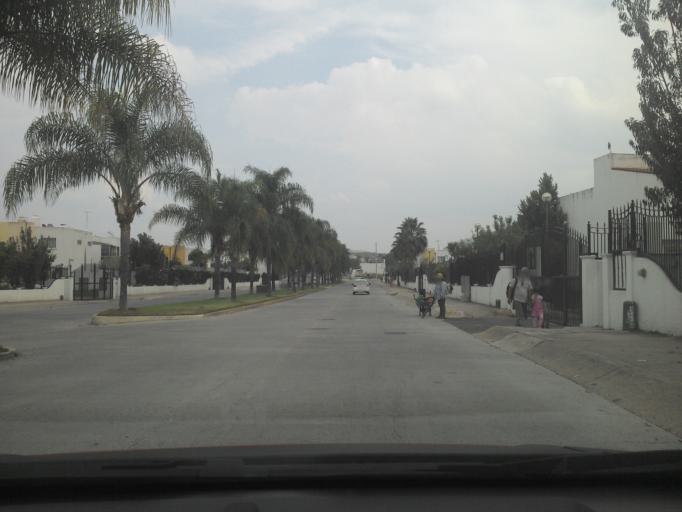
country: MX
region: Jalisco
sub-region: Tlajomulco de Zuniga
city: Lomas de San Agustin
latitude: 20.5307
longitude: -103.4711
